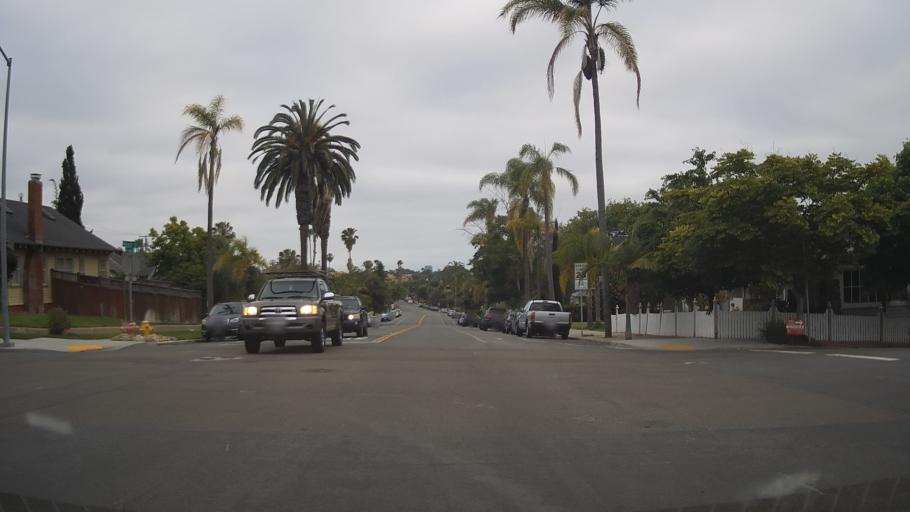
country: US
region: California
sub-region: San Diego County
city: San Diego
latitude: 32.7574
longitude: -117.1513
